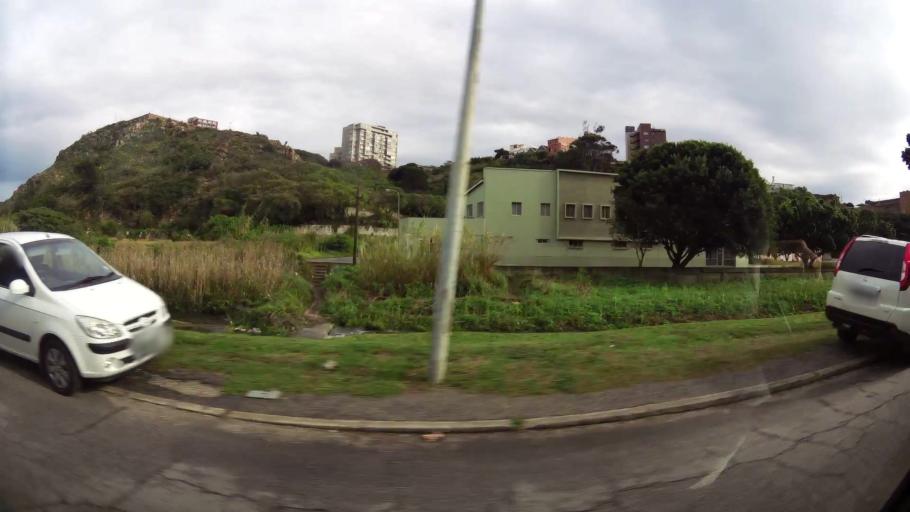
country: ZA
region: Eastern Cape
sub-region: Nelson Mandela Bay Metropolitan Municipality
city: Port Elizabeth
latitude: -33.9664
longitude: 25.6237
